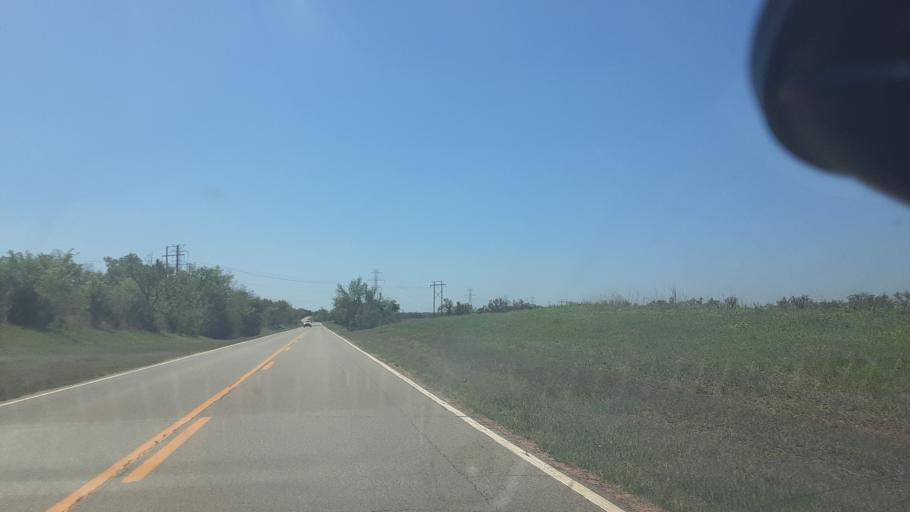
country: US
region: Oklahoma
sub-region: Logan County
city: Langston
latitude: 36.0992
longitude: -97.3940
